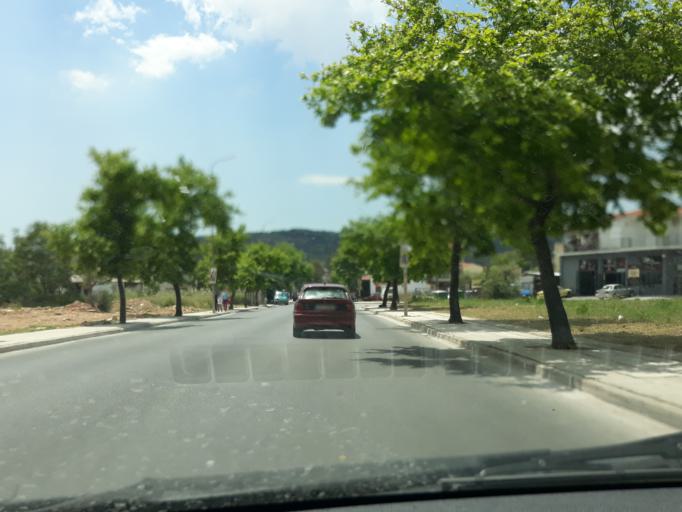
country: GR
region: Attica
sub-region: Nomarchia Dytikis Attikis
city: Ano Liosia
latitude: 38.0763
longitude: 23.7079
